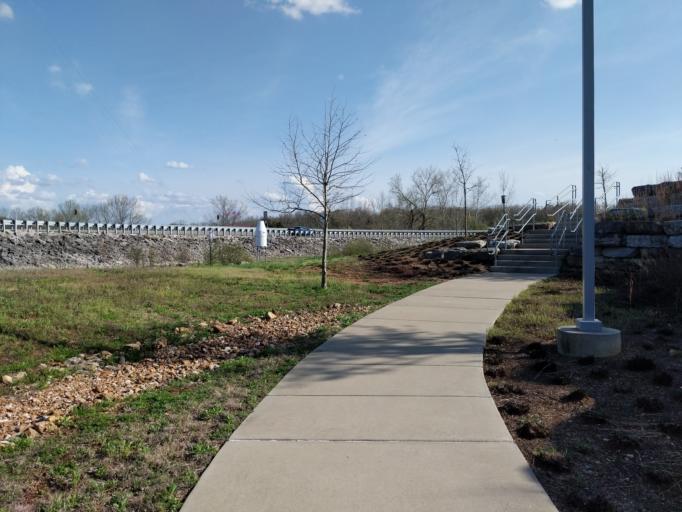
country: US
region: Missouri
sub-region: Taney County
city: Hollister
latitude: 36.5939
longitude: -93.3119
